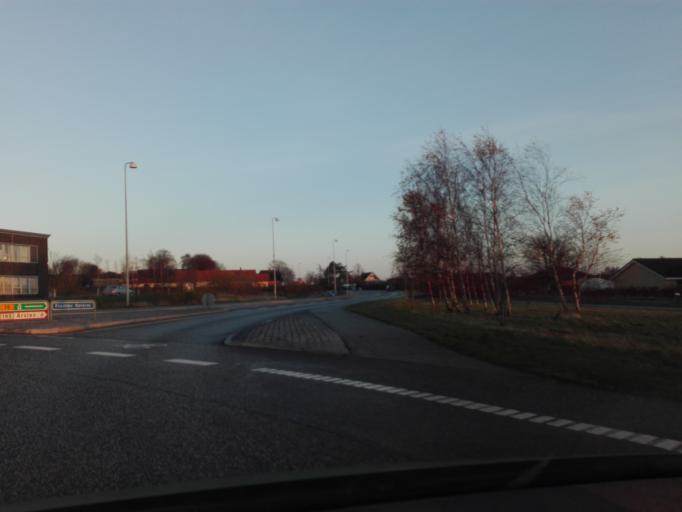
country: DK
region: Central Jutland
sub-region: Arhus Kommune
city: Framlev
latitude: 56.1519
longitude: 10.0000
